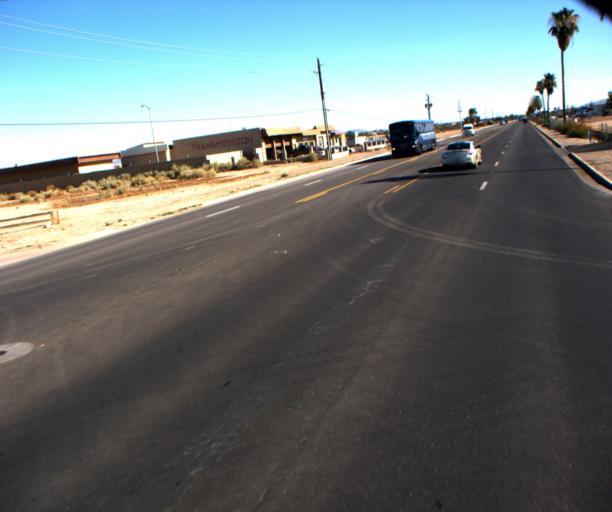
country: US
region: Arizona
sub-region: Pinal County
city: Casa Grande
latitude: 32.8978
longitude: -111.7572
